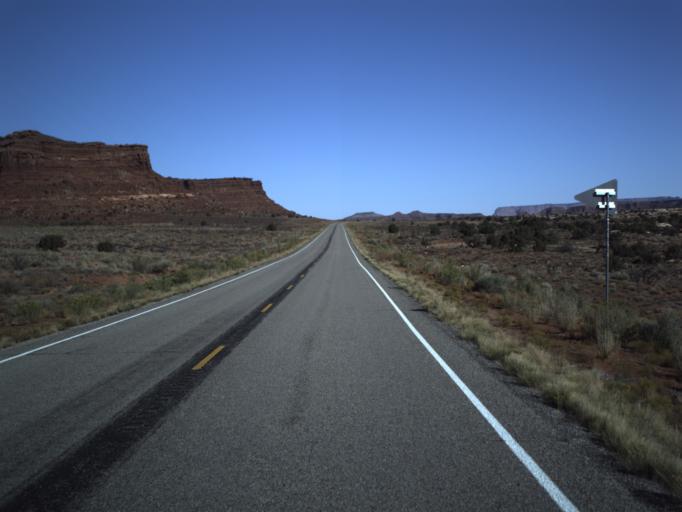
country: US
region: Utah
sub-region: San Juan County
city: Blanding
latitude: 37.7601
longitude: -110.2832
